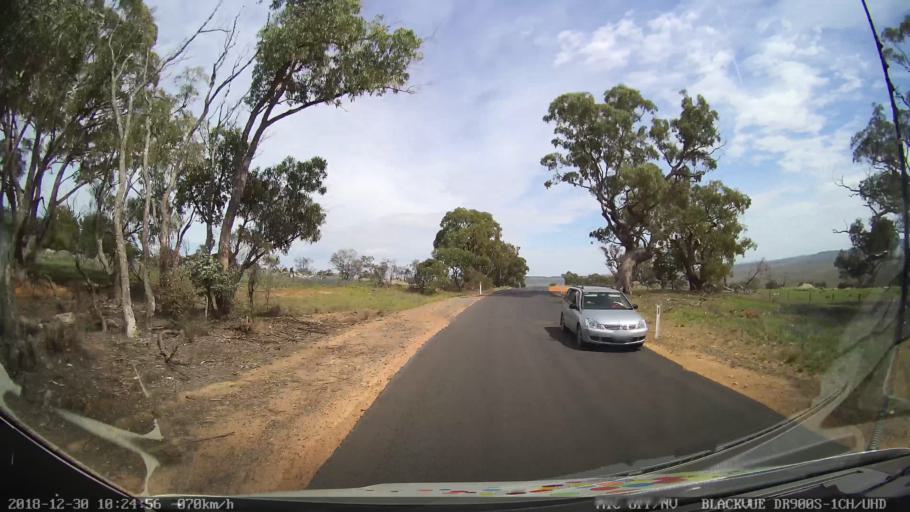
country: AU
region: New South Wales
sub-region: Snowy River
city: Berridale
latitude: -36.5303
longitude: 148.9630
